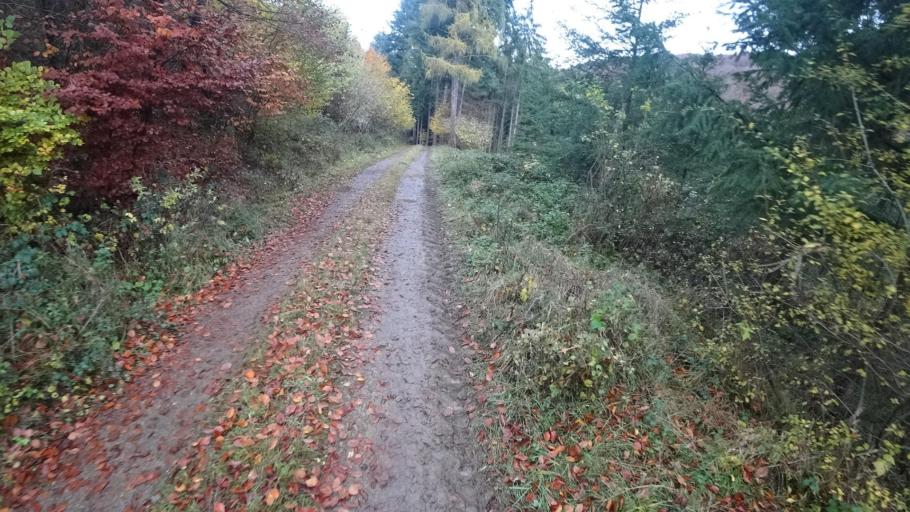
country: DE
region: Rheinland-Pfalz
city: Badenhard
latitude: 50.1147
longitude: 7.6436
